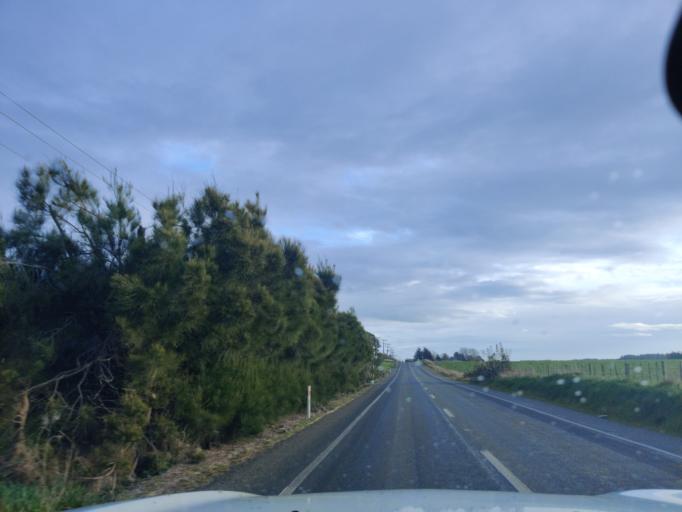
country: NZ
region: Manawatu-Wanganui
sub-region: Palmerston North City
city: Palmerston North
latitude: -40.3965
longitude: 175.6265
